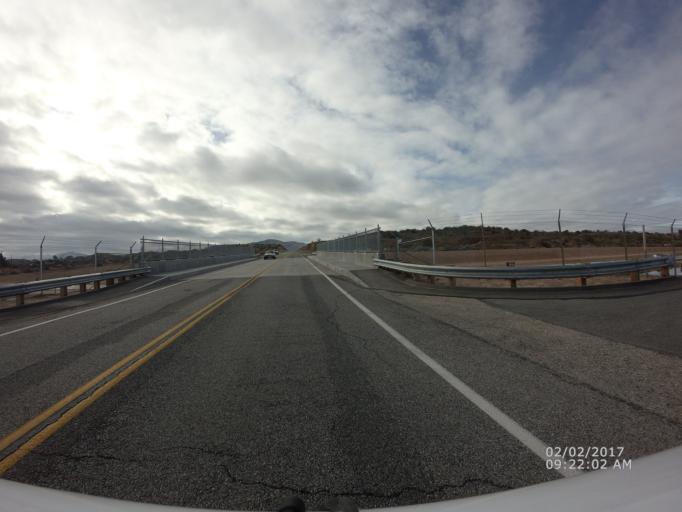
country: US
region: California
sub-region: Los Angeles County
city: Vincent
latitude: 34.5327
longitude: -118.0585
